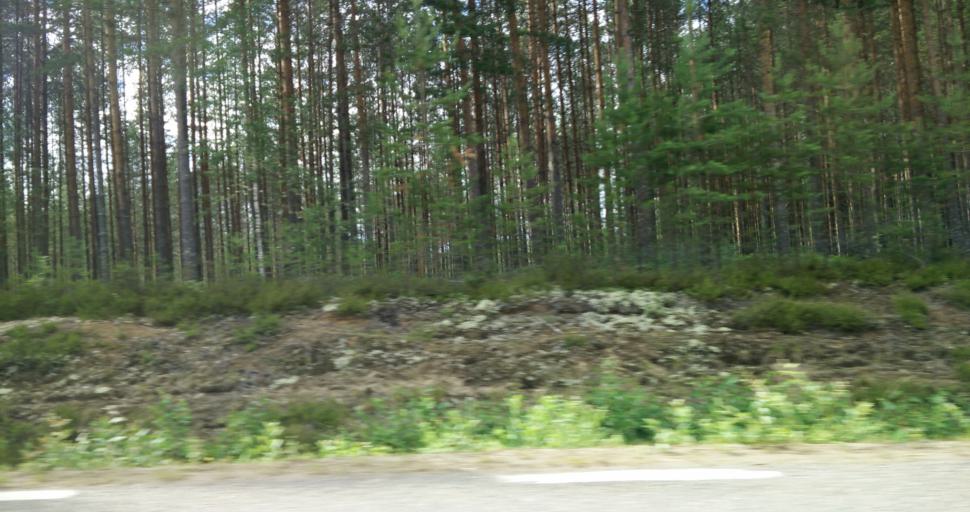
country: SE
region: Vaermland
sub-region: Hagfors Kommun
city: Ekshaerad
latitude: 60.0441
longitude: 13.5225
